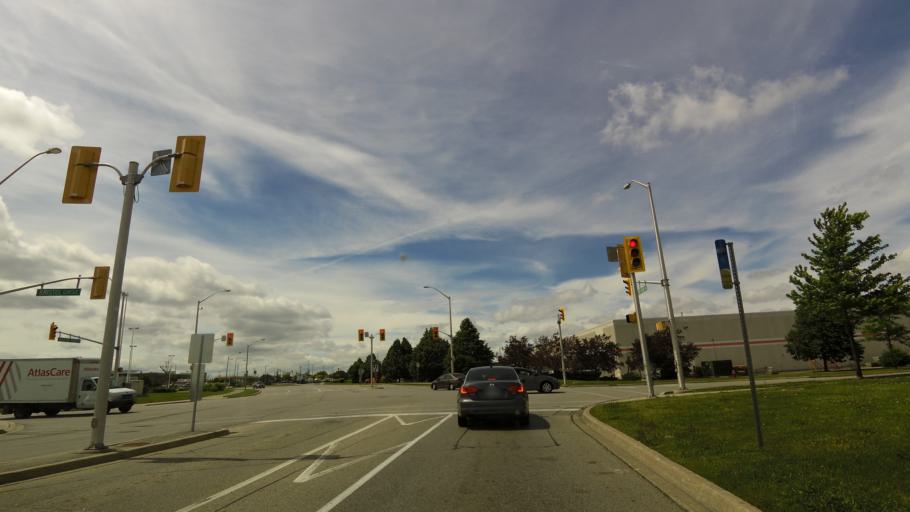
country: CA
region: Ontario
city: Oakville
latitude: 43.5169
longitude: -79.6841
